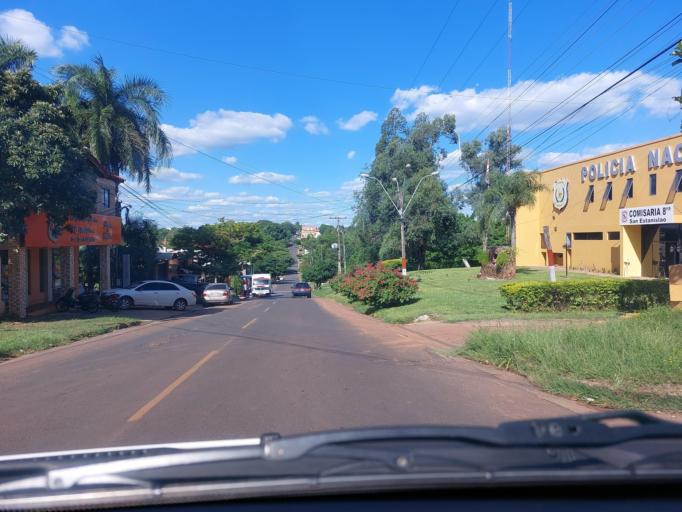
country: PY
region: San Pedro
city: Guayaybi
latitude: -24.6646
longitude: -56.4505
